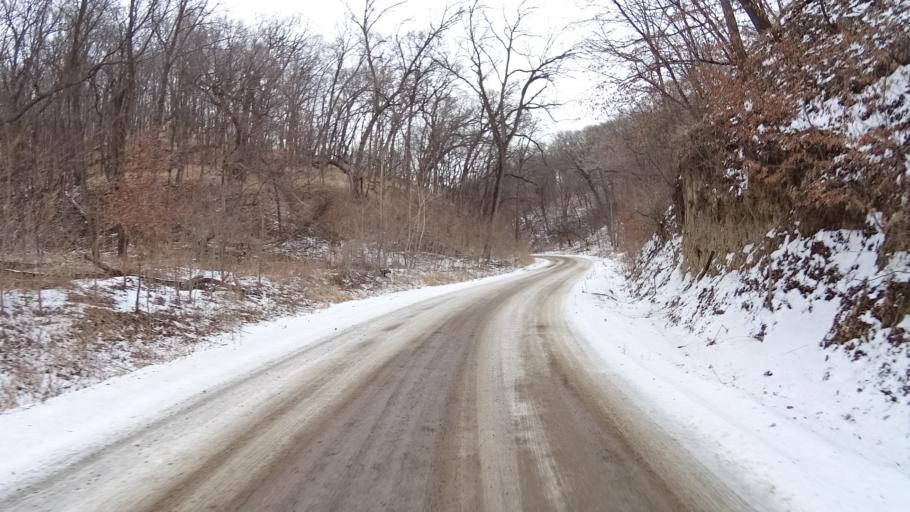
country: US
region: Nebraska
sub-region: Sarpy County
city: Bellevue
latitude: 41.1711
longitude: -95.8985
